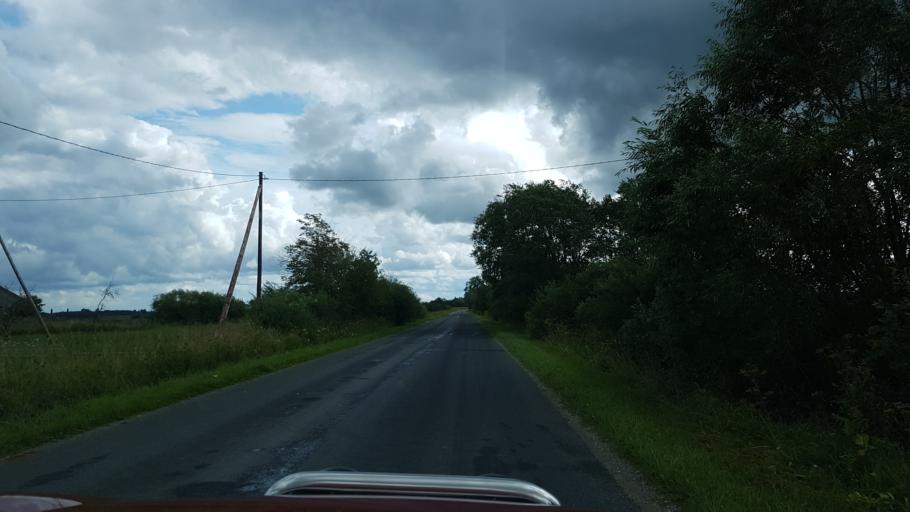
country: EE
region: Laeaene
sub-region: Lihula vald
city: Lihula
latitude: 58.7176
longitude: 23.9874
